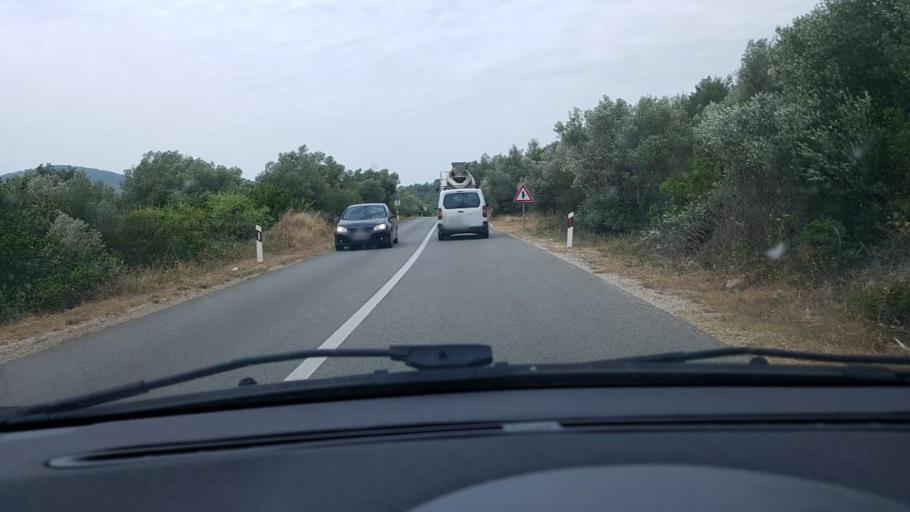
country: HR
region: Dubrovacko-Neretvanska
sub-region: Grad Dubrovnik
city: Vela Luka
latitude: 42.9498
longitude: 16.7588
